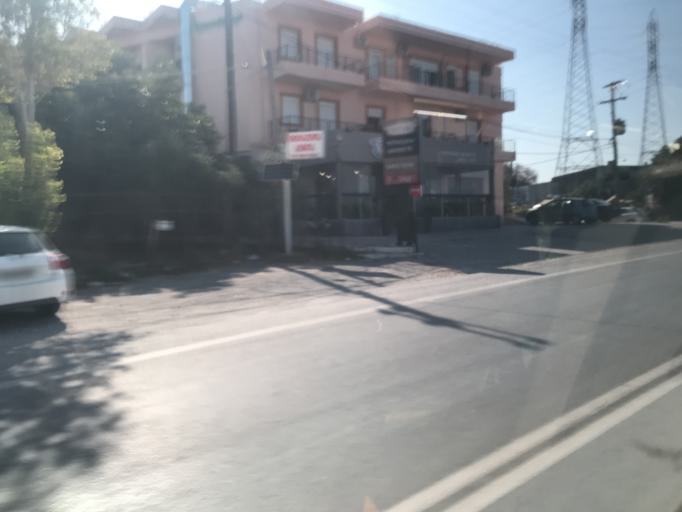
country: GR
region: Crete
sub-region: Nomos Irakleiou
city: Gazi
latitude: 35.3084
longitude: 25.0901
